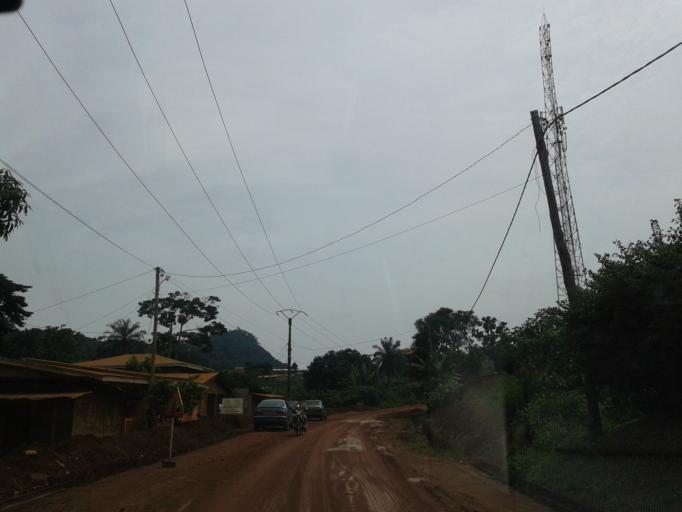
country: CM
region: Centre
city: Yaounde
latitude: 3.9238
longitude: 11.5127
